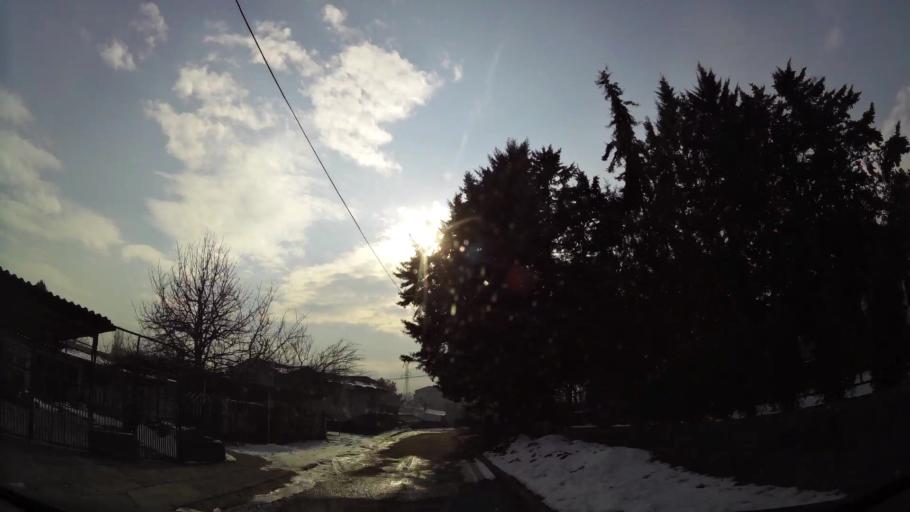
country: MK
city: Creshevo
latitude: 42.0076
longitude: 21.5017
